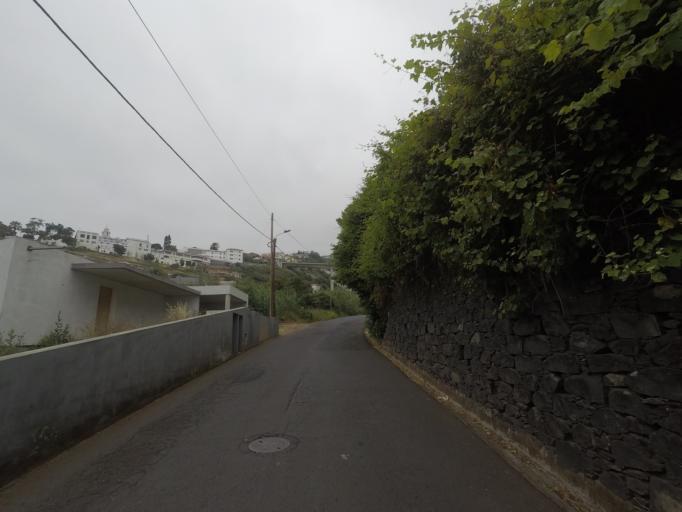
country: PT
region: Madeira
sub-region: Funchal
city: Nossa Senhora do Monte
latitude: 32.6755
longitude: -16.9437
